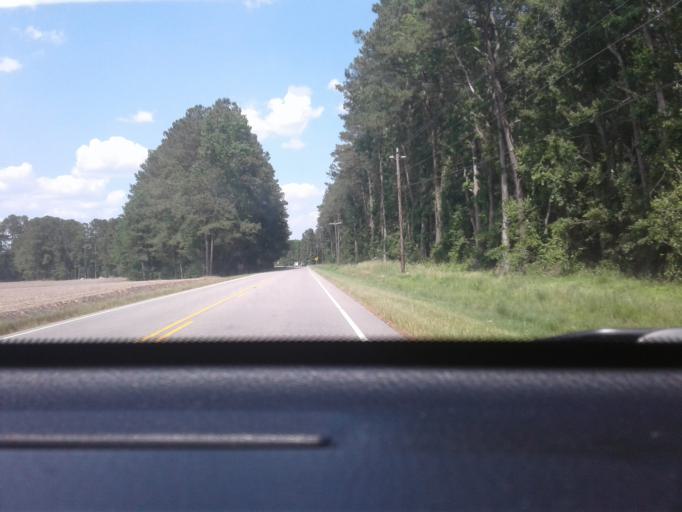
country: US
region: North Carolina
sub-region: Cumberland County
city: Eastover
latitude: 35.1830
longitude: -78.7054
